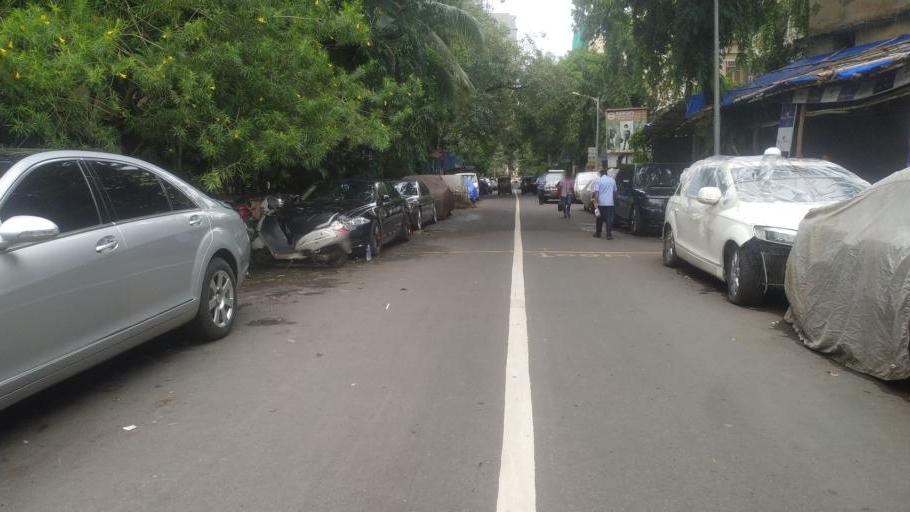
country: IN
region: Maharashtra
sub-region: Mumbai Suburban
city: Mumbai
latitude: 19.0651
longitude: 72.8362
